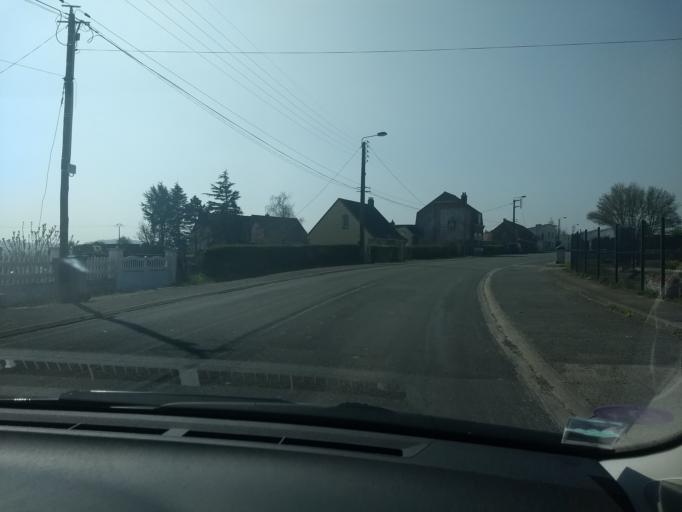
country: FR
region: Nord-Pas-de-Calais
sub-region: Departement du Pas-de-Calais
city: Tatinghem
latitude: 50.7403
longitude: 2.2020
